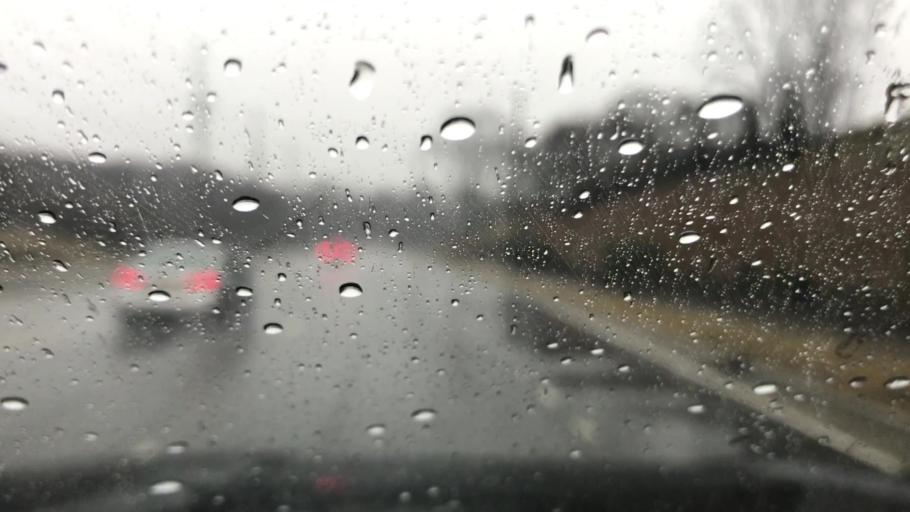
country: US
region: Tennessee
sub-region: Williamson County
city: Nolensville
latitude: 36.0453
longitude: -86.6854
